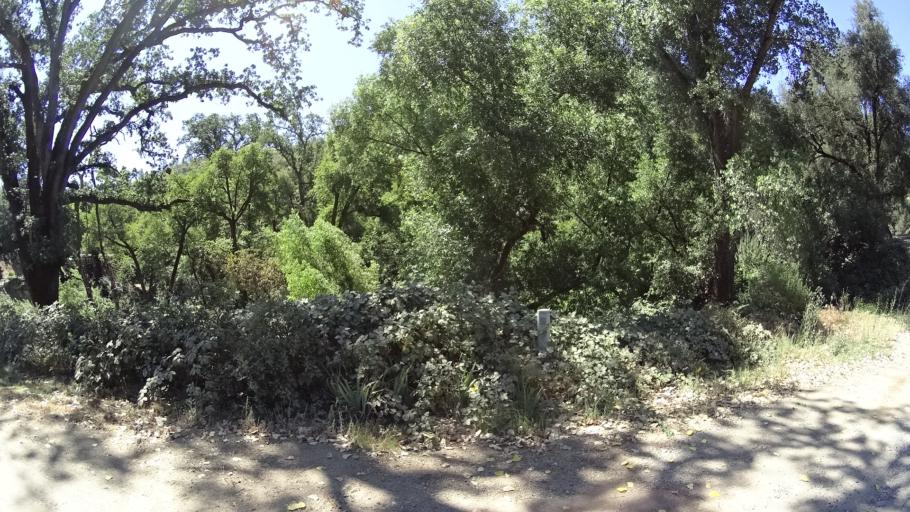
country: US
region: California
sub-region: Calaveras County
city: San Andreas
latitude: 38.2041
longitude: -120.6440
